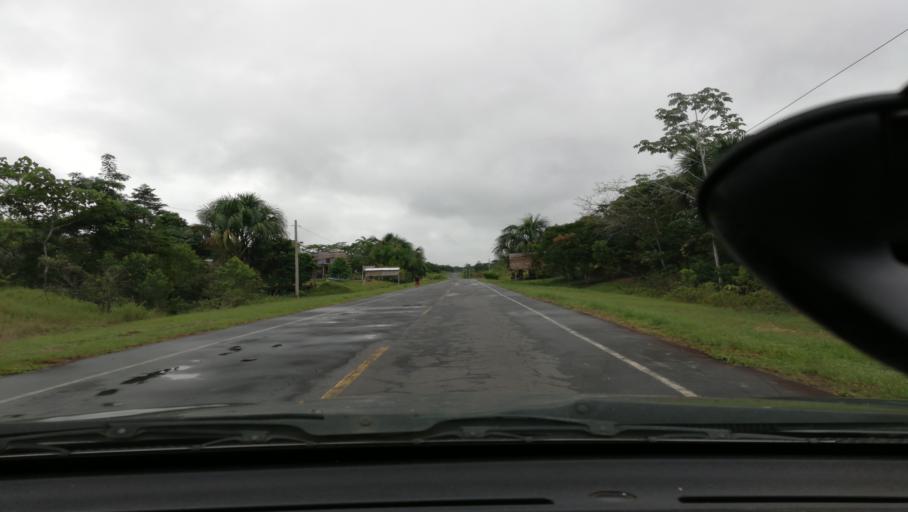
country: PE
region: Loreto
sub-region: Provincia de Loreto
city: Nauta
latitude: -4.3414
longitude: -73.5388
